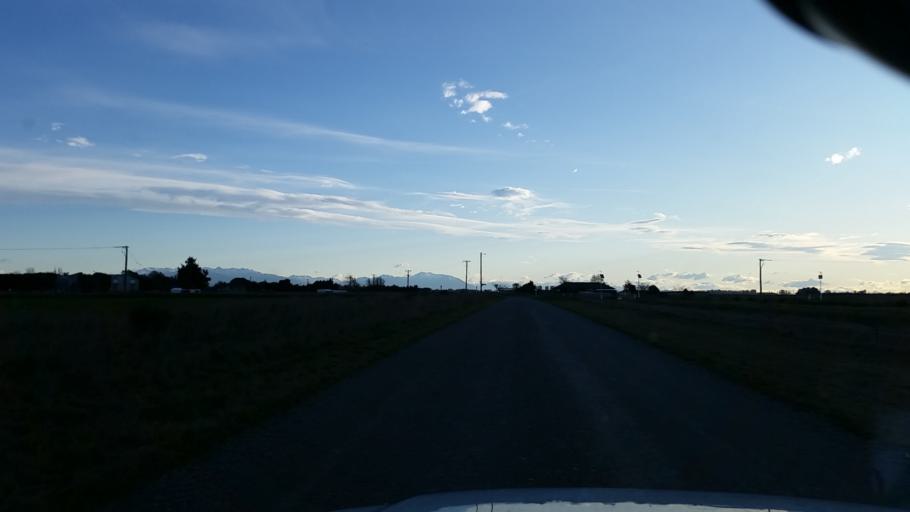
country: NZ
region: Canterbury
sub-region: Ashburton District
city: Tinwald
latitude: -43.9773
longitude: 171.5080
